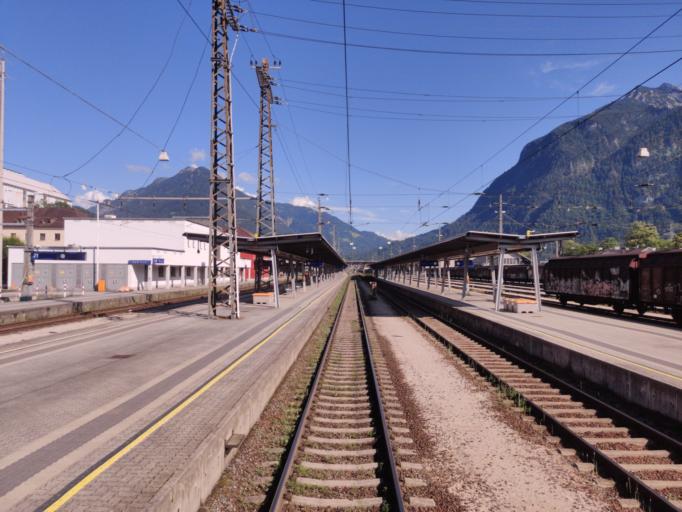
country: AT
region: Vorarlberg
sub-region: Politischer Bezirk Bludenz
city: Bludenz
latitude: 47.1560
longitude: 9.8131
